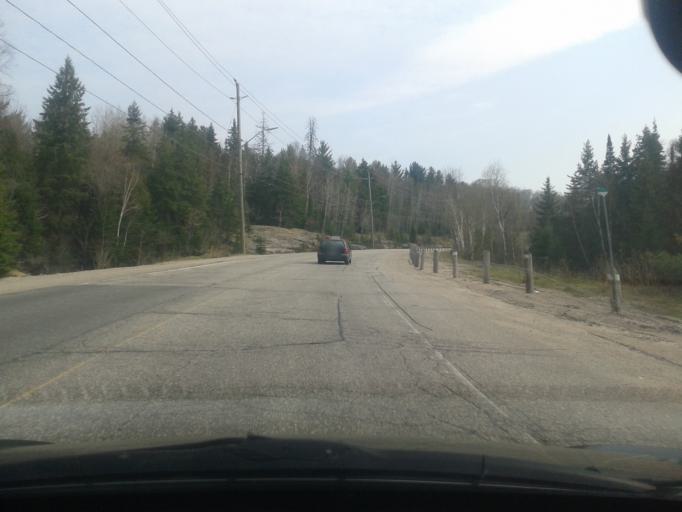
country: CA
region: Ontario
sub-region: Nipissing District
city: North Bay
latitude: 46.3383
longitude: -79.4943
